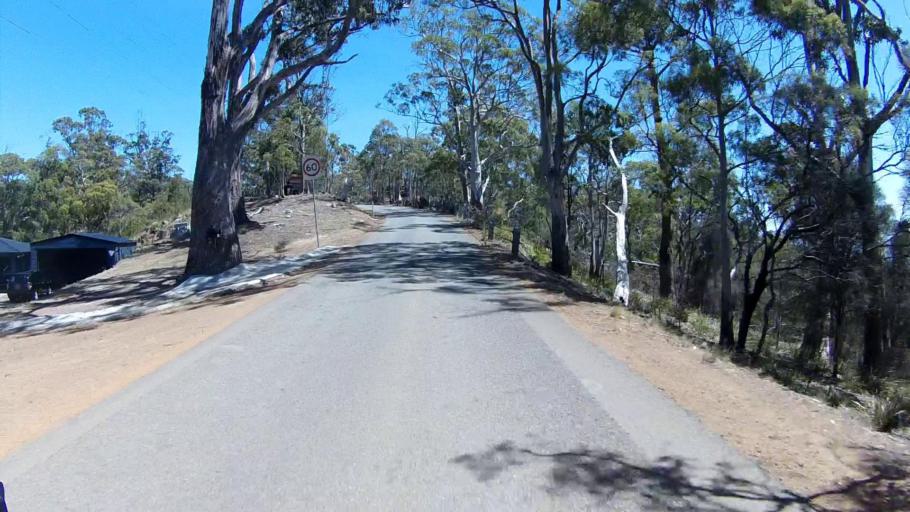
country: AU
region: Tasmania
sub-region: Clarence
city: Cambridge
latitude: -42.8599
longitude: 147.4504
